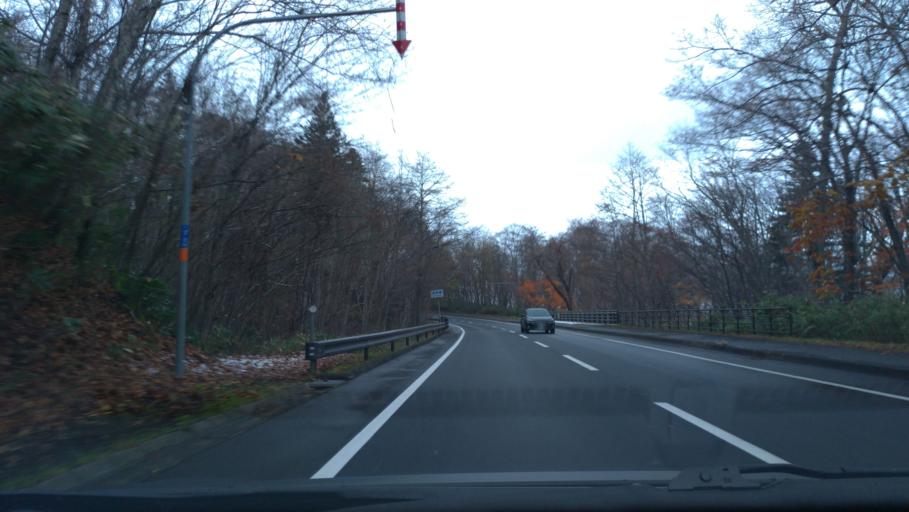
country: JP
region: Hokkaido
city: Shiraoi
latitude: 42.7368
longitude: 141.3604
